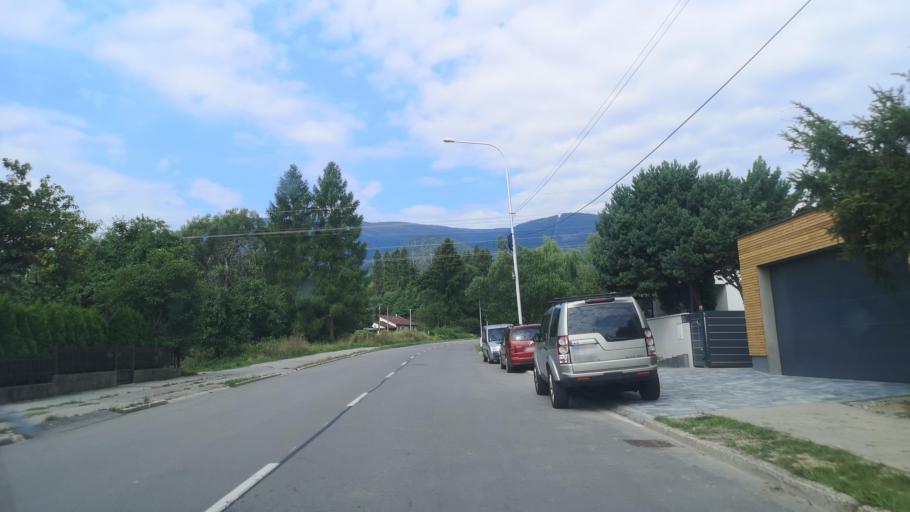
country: SK
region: Zilinsky
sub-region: Okres Martin
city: Martin
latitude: 49.0804
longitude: 18.8935
